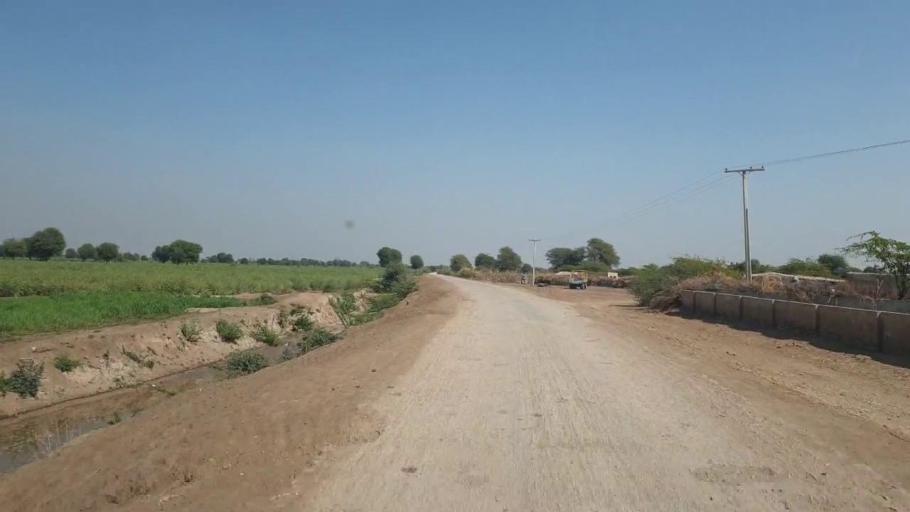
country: PK
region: Sindh
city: Digri
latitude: 25.0913
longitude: 69.2342
